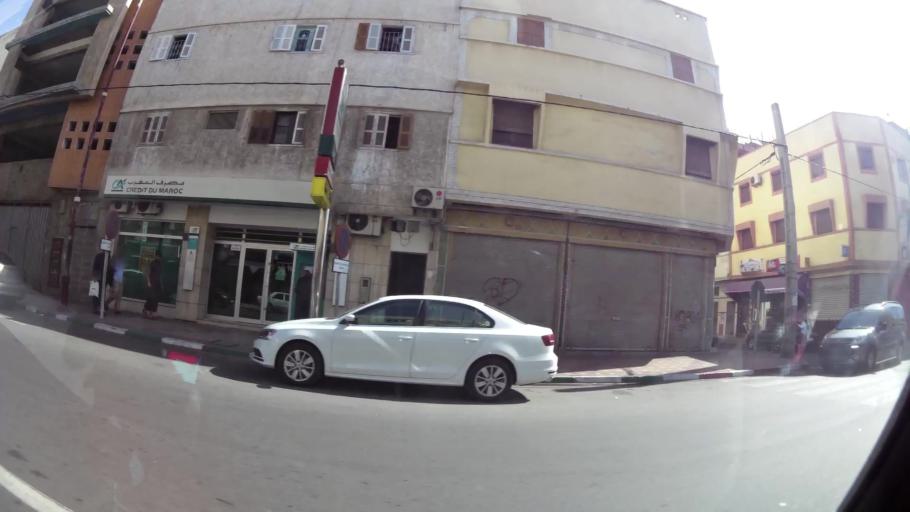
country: MA
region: Souss-Massa-Draa
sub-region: Inezgane-Ait Mellou
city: Inezgane
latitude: 30.3718
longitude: -9.5490
